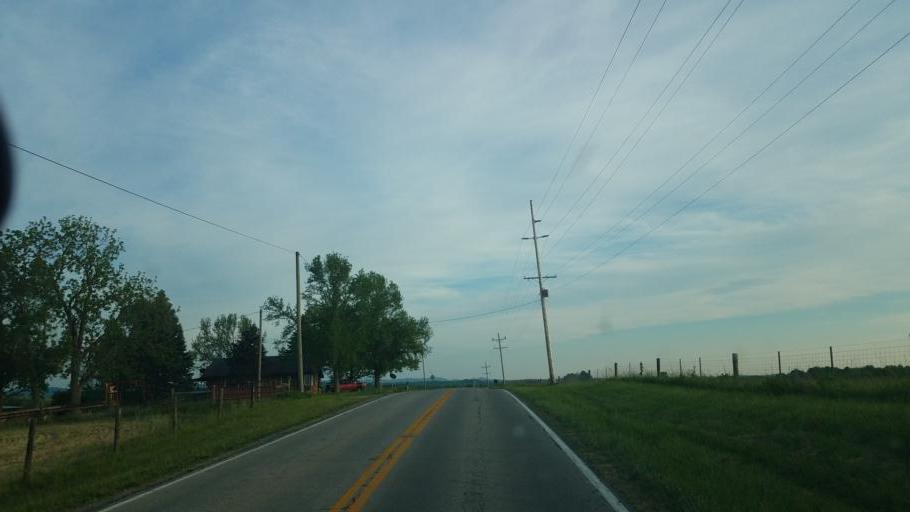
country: US
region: Ohio
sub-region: Highland County
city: Greenfield
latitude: 39.3002
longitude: -83.4088
